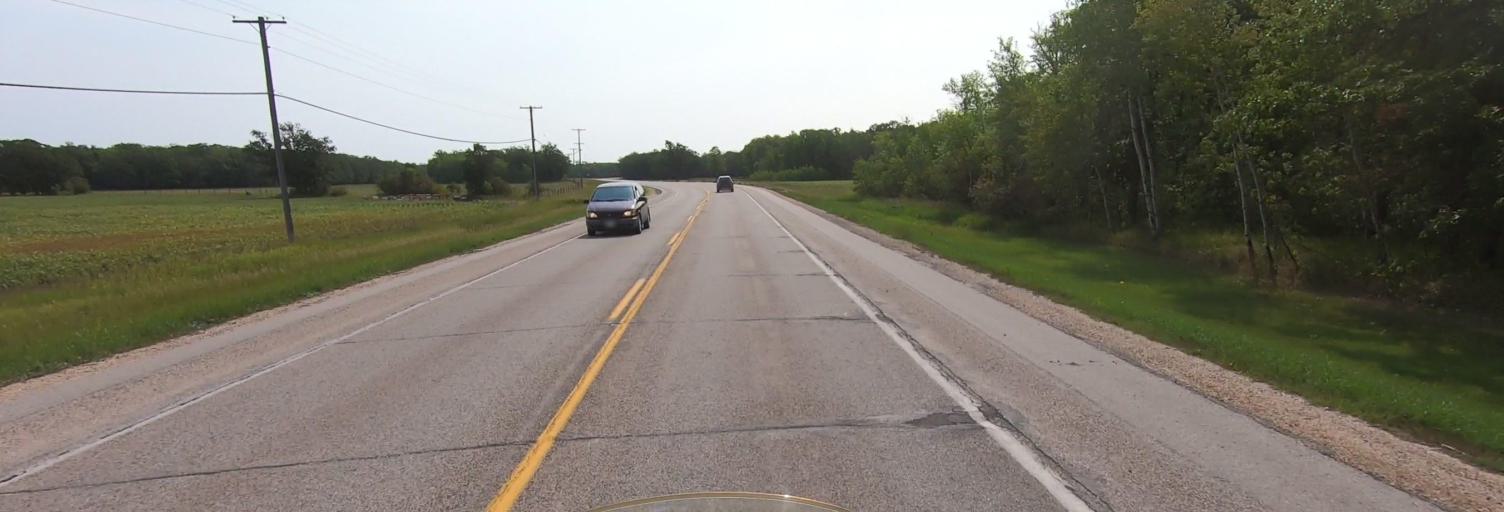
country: CA
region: Manitoba
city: Niverville
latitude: 49.7373
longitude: -97.1148
